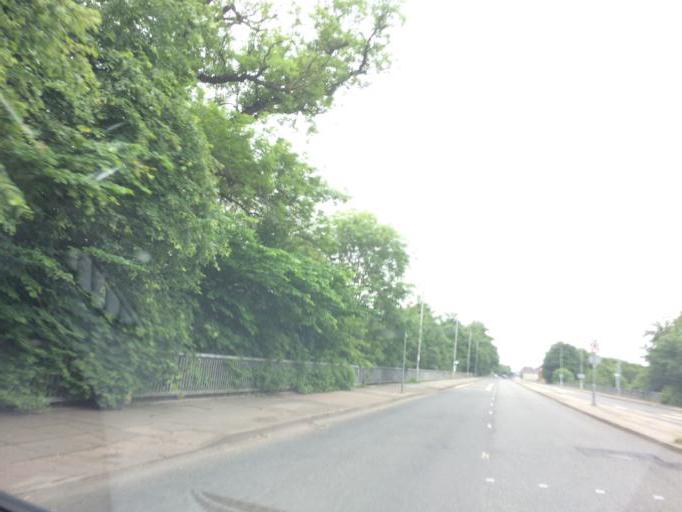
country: GB
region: Scotland
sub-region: East Renfrewshire
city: Giffnock
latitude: 55.8497
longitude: -4.3112
